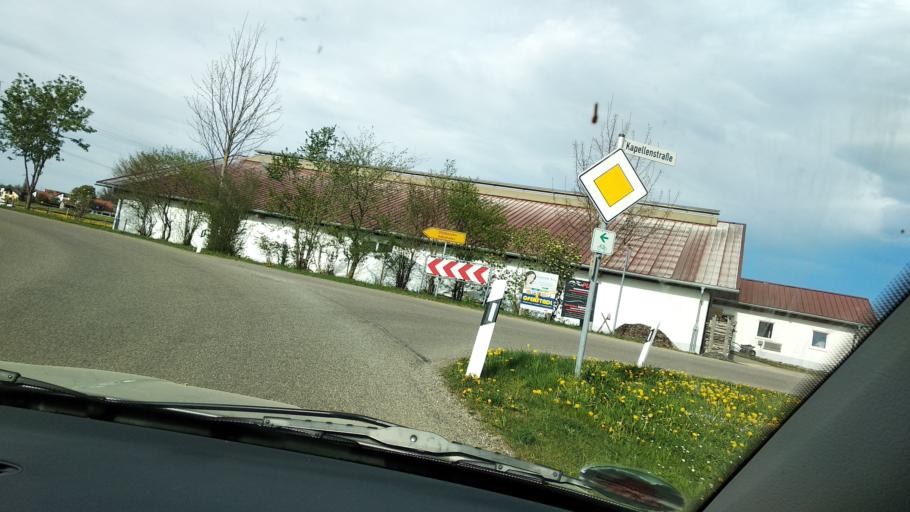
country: DE
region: Bavaria
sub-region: Swabia
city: Lachen
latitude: 47.9313
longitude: 10.2317
